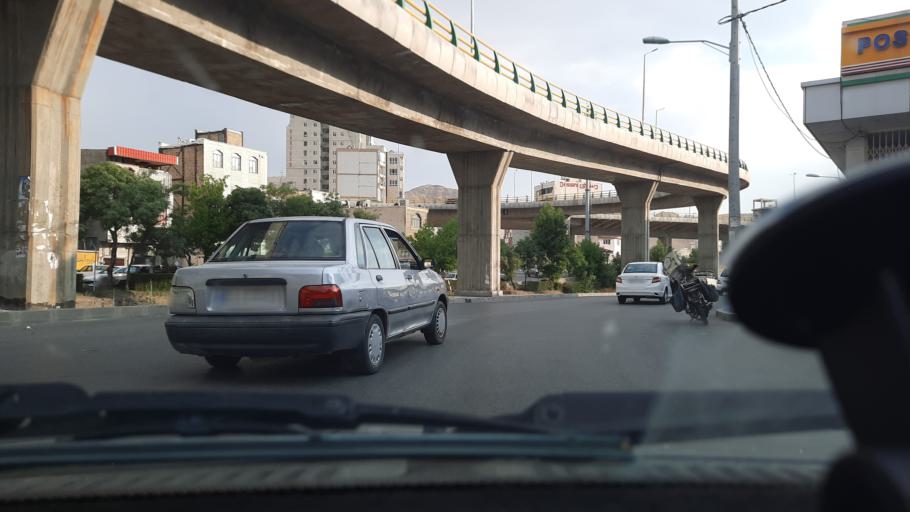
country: IR
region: Markazi
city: Arak
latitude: 34.0788
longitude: 49.6773
